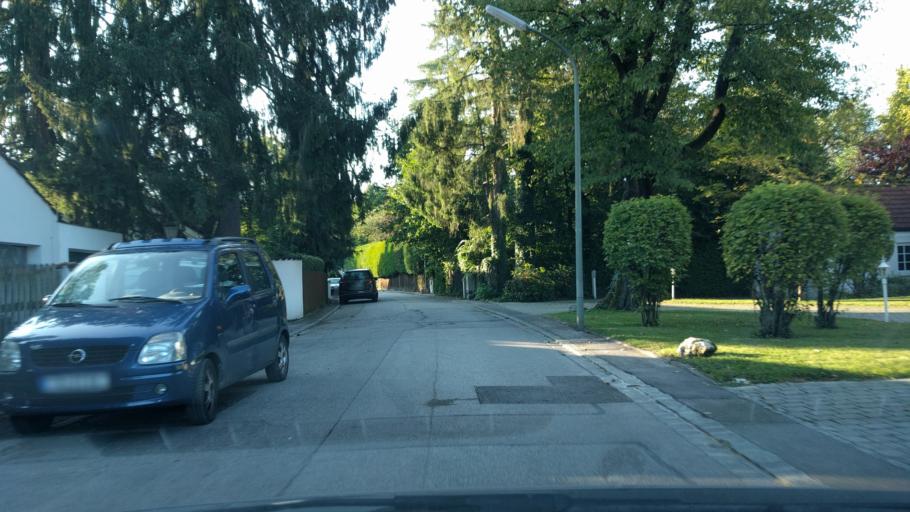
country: DE
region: Bavaria
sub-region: Upper Bavaria
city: Grunwald
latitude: 48.0446
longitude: 11.5339
